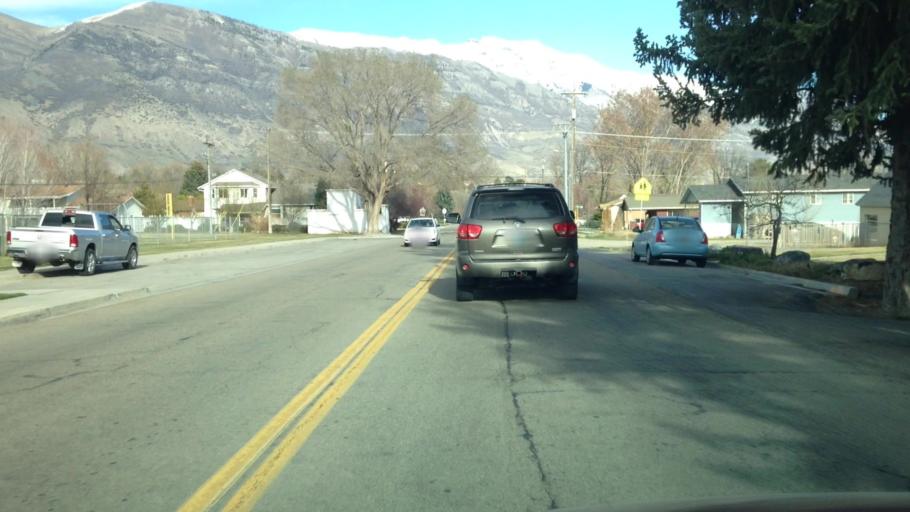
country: US
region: Utah
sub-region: Utah County
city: American Fork
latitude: 40.3918
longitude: -111.7838
